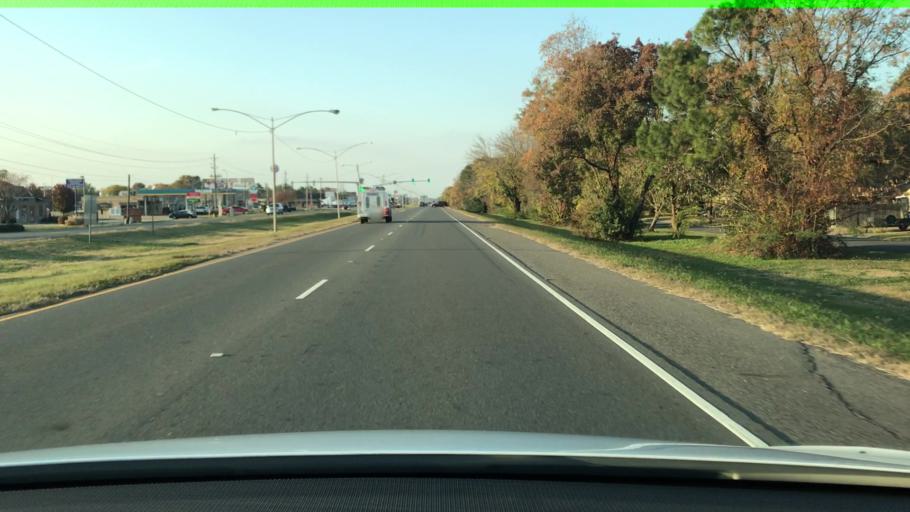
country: US
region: Louisiana
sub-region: Bossier Parish
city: Bossier City
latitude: 32.4189
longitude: -93.7042
